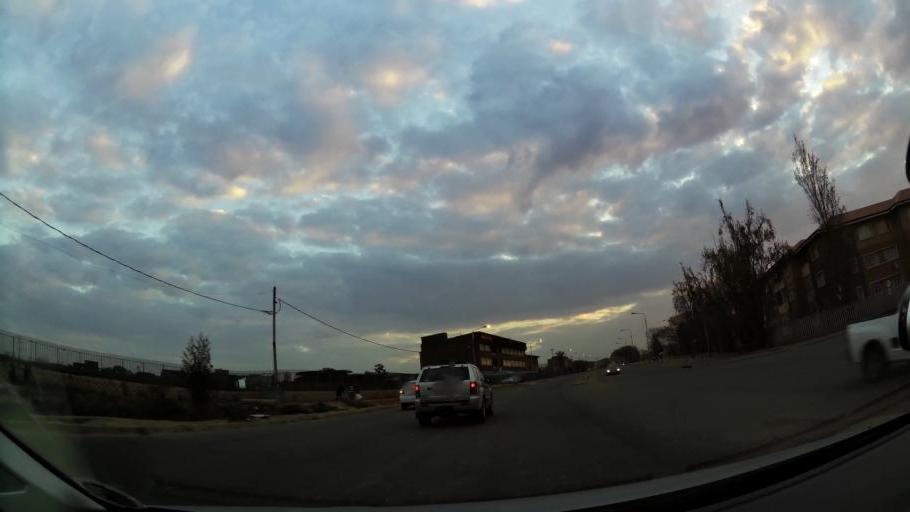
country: ZA
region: Gauteng
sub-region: Ekurhuleni Metropolitan Municipality
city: Germiston
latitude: -26.2039
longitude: 28.1321
